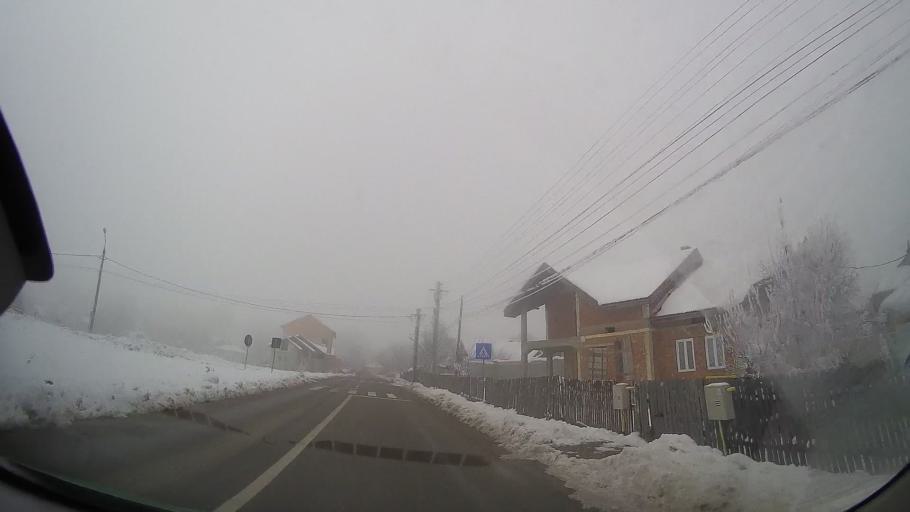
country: RO
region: Iasi
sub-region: Municipiul Pascani
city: Pascani
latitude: 47.2587
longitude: 26.7076
